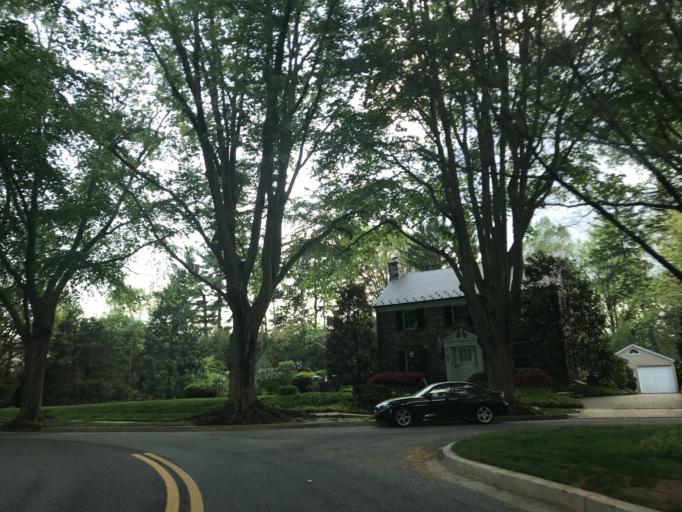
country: US
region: Maryland
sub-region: Baltimore County
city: Towson
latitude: 39.3733
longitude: -76.6217
